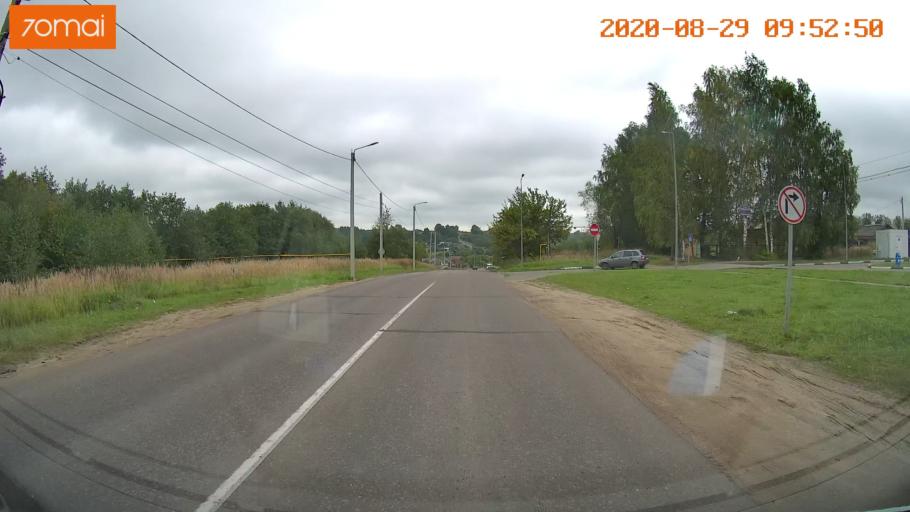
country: RU
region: Ivanovo
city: Zarechnyy
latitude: 57.4231
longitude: 42.2132
